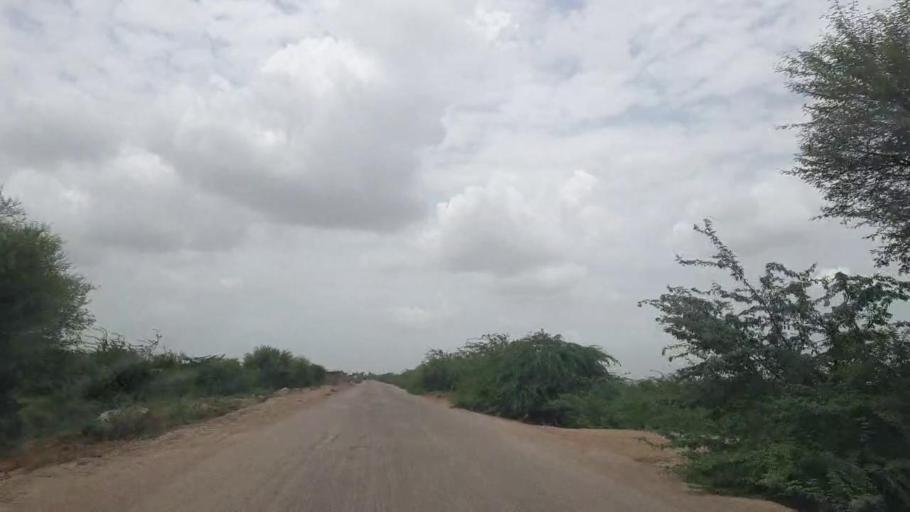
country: PK
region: Sindh
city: Naukot
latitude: 24.9222
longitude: 69.2736
